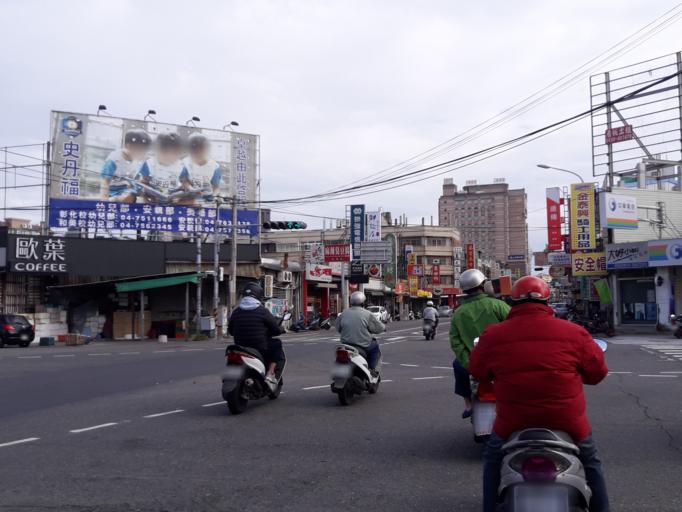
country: TW
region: Taiwan
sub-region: Changhua
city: Chang-hua
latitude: 24.0906
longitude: 120.5355
